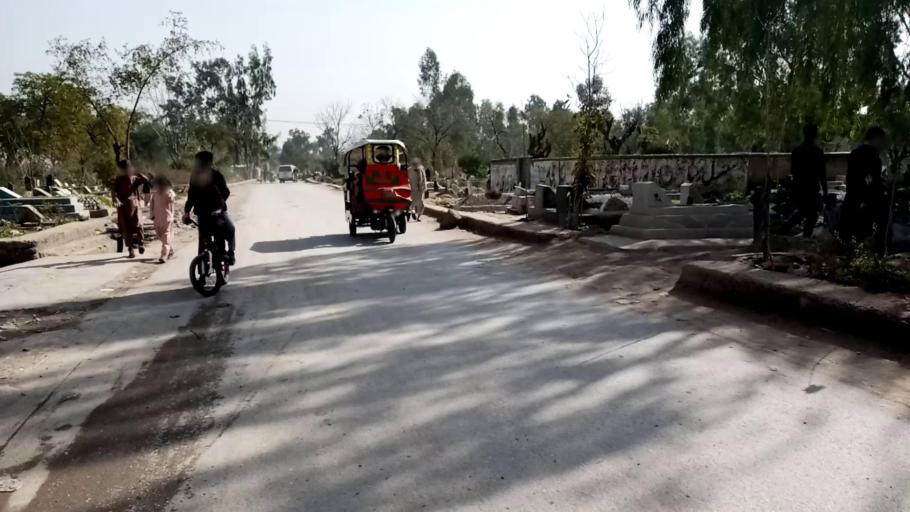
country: PK
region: Khyber Pakhtunkhwa
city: Peshawar
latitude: 33.9964
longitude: 71.5846
